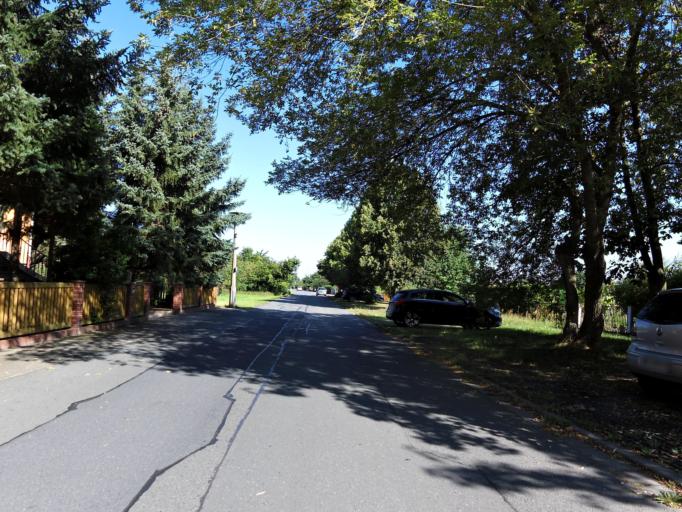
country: DE
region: Saxony
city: Riesa
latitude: 51.3266
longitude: 13.2973
